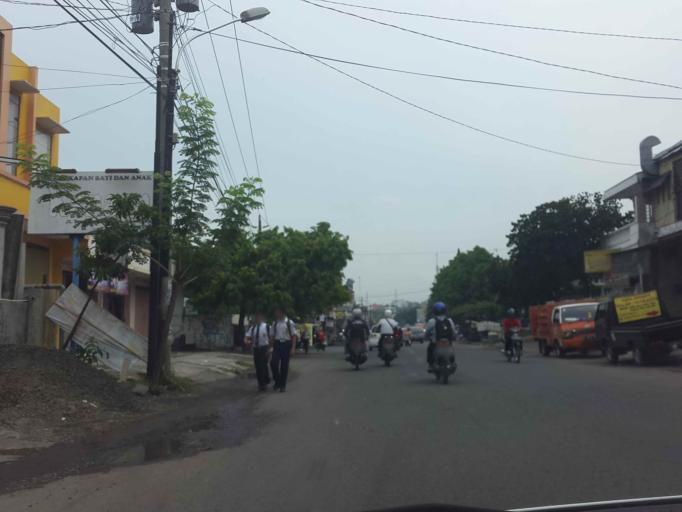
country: ID
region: Central Java
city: Semarang
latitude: -7.0097
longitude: 110.4381
